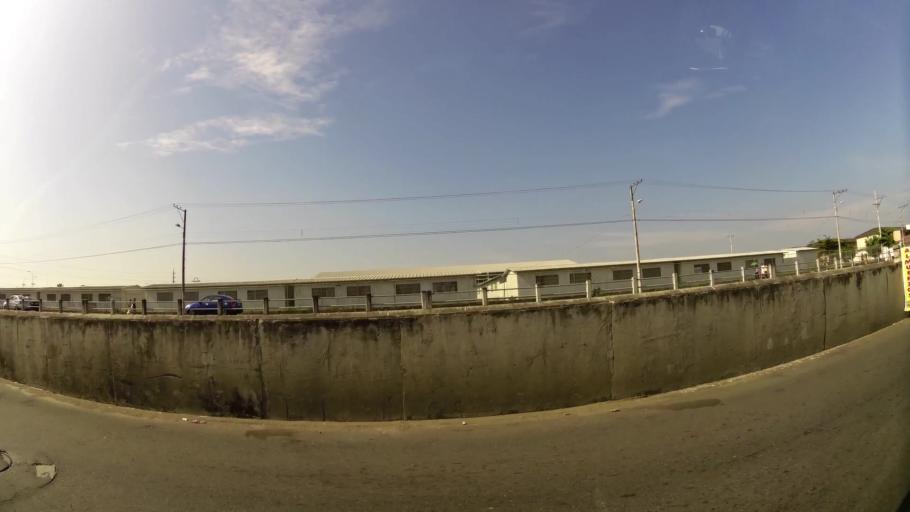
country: EC
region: Guayas
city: Eloy Alfaro
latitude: -2.0926
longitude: -79.9140
